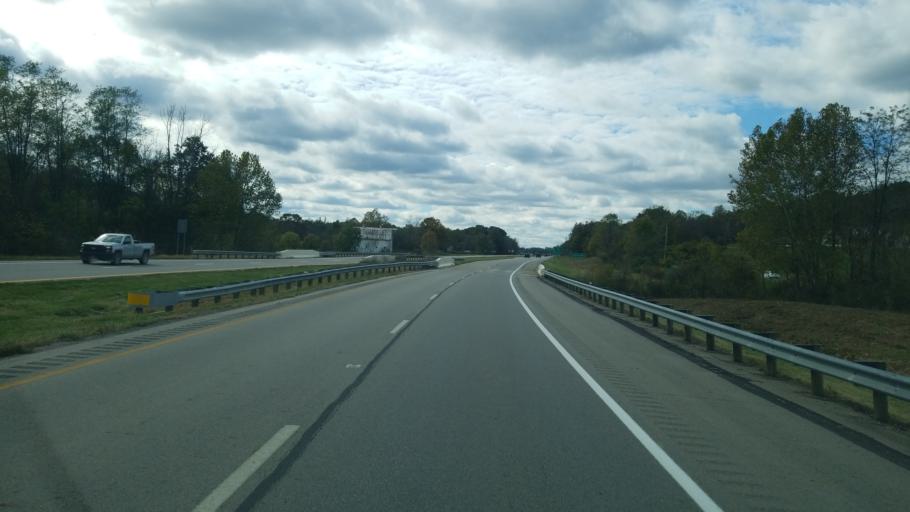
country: US
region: Ohio
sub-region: Jackson County
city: Jackson
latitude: 39.0514
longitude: -82.5978
